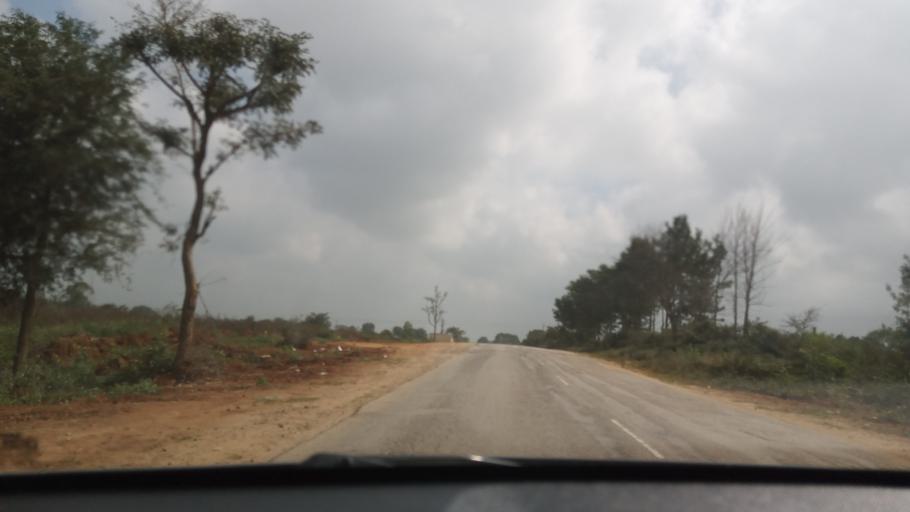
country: IN
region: Karnataka
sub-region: Kolar
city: Srinivaspur
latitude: 13.4406
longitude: 78.2278
